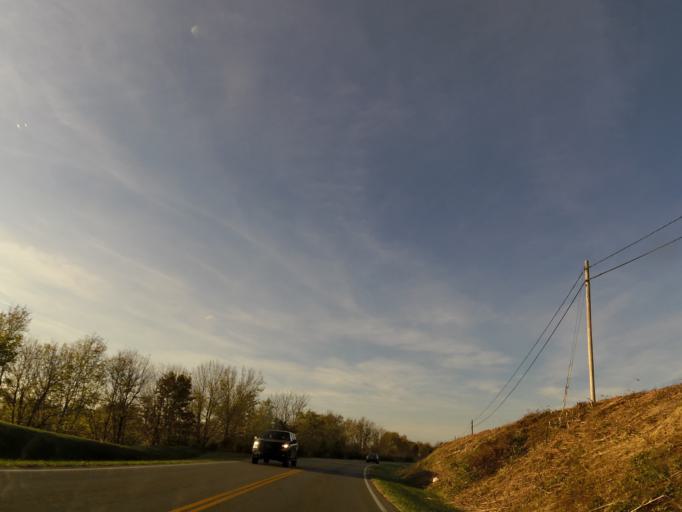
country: US
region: Kentucky
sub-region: Garrard County
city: Lancaster
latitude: 37.6432
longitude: -84.5941
